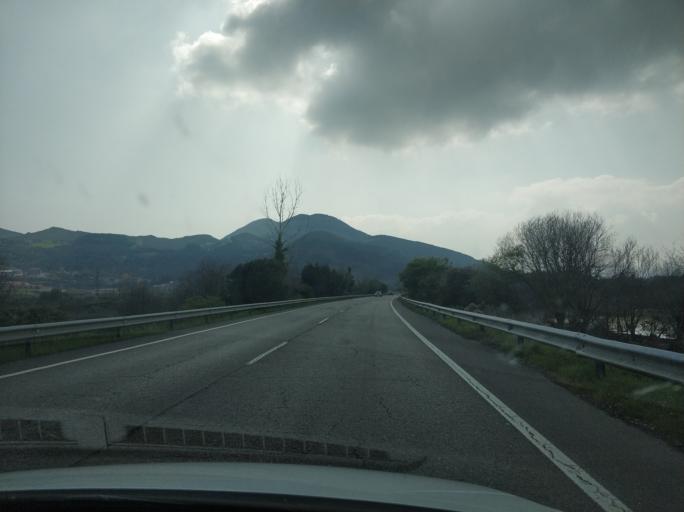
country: ES
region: Cantabria
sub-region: Provincia de Cantabria
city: Santona
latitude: 43.4590
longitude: -3.4668
